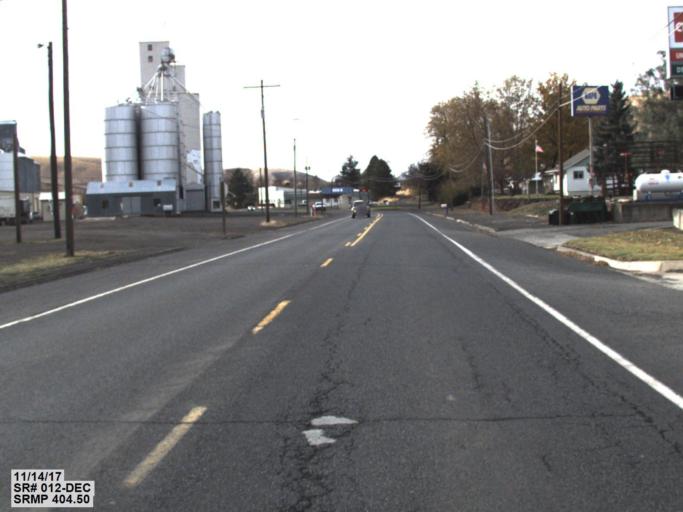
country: US
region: Washington
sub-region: Garfield County
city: Pomeroy
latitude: 46.4748
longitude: -117.5790
